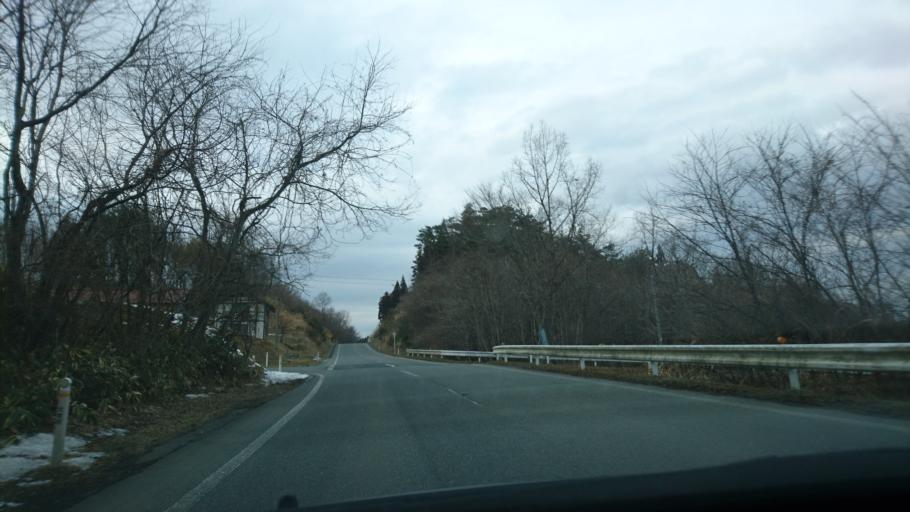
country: JP
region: Iwate
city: Ichinoseki
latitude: 38.9737
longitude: 141.3559
